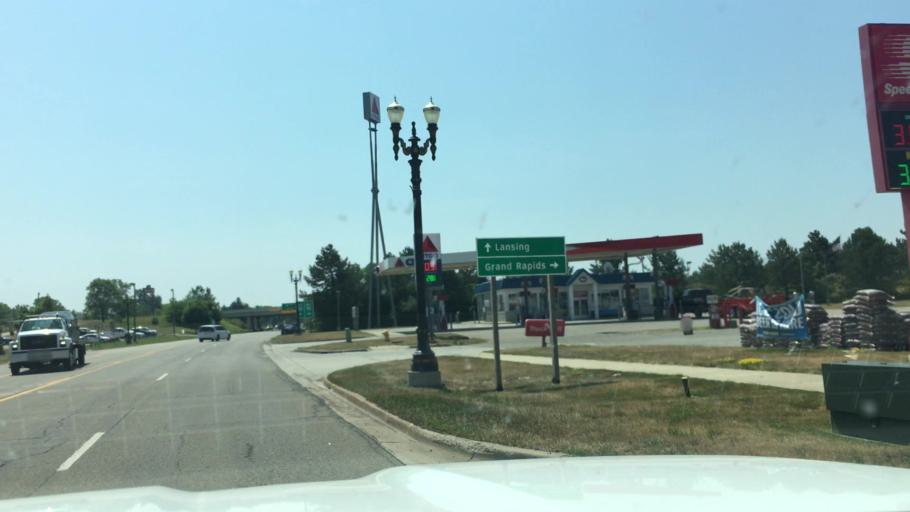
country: US
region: Michigan
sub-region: Ionia County
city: Portland
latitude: 42.8619
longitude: -84.8865
